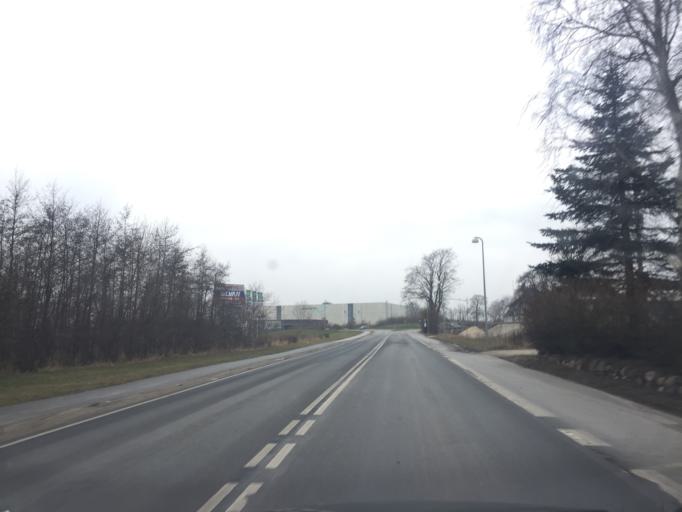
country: DK
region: Zealand
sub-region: Greve Kommune
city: Greve
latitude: 55.5932
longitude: 12.2707
